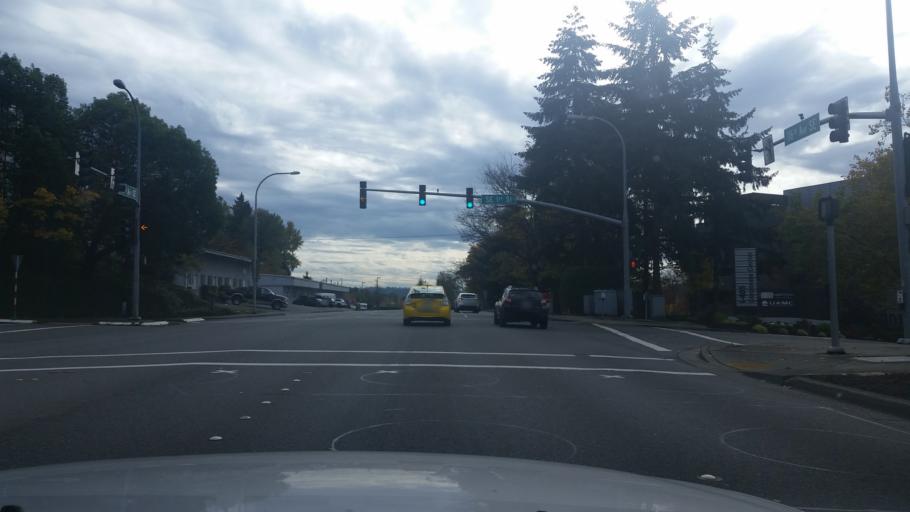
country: US
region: Washington
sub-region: King County
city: Bellevue
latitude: 47.6086
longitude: -122.1856
